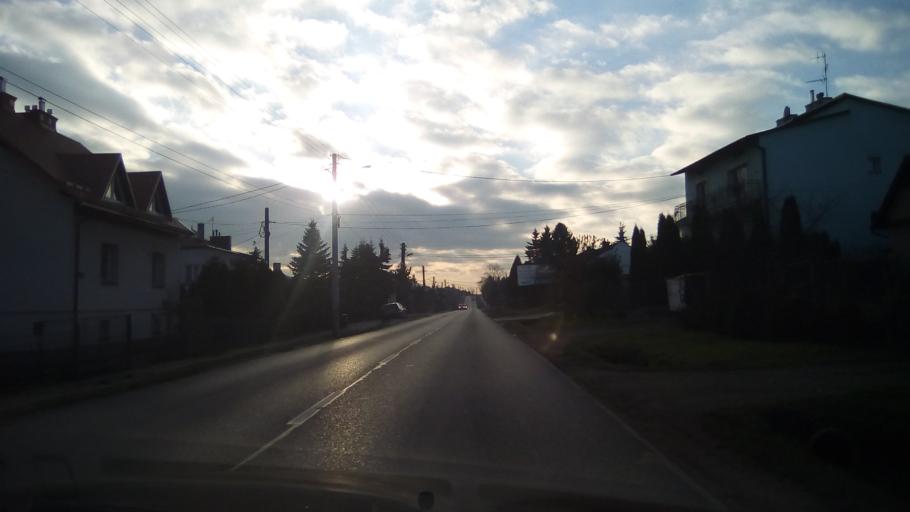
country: PL
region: Subcarpathian Voivodeship
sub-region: Rzeszow
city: Przybyszowka
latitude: 50.0470
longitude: 21.9258
